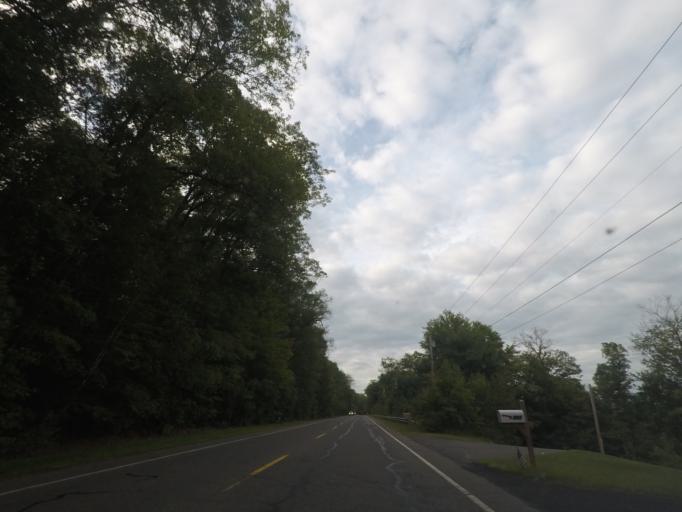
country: US
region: Massachusetts
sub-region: Hampden County
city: Palmer
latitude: 42.1943
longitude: -72.2675
